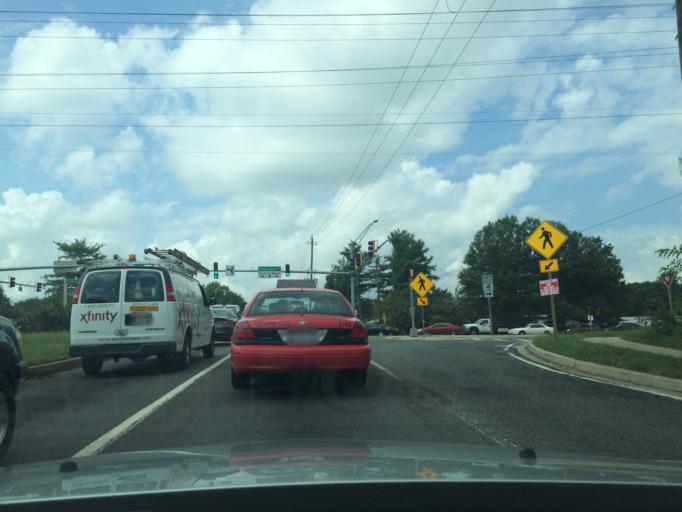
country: US
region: Maryland
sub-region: Prince George's County
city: Coral Hills
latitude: 38.8607
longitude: -76.9183
